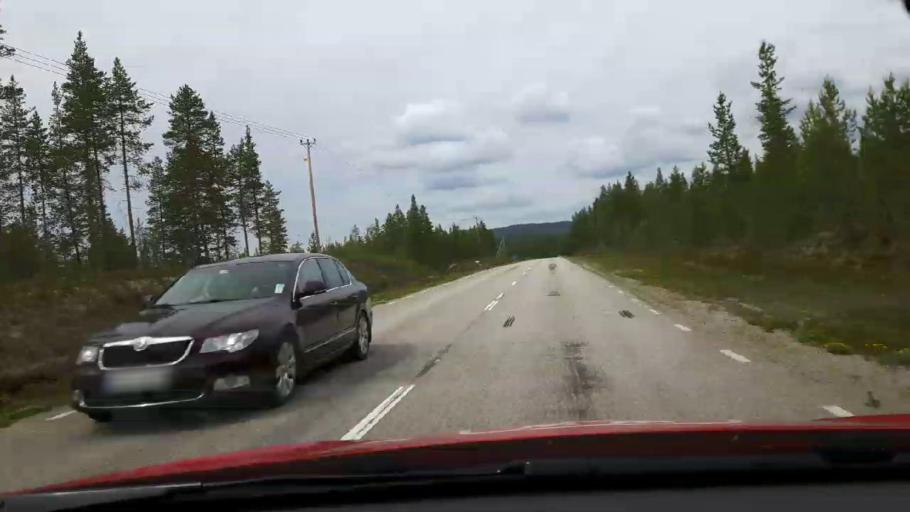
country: SE
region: Jaemtland
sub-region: Harjedalens Kommun
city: Sveg
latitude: 62.4006
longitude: 13.7426
